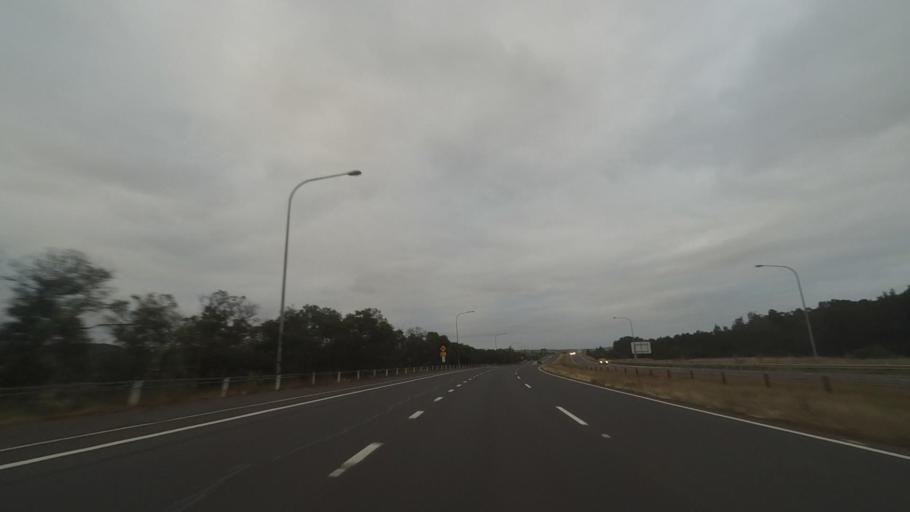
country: AU
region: New South Wales
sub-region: Shellharbour
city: Croom
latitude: -34.6122
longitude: 150.8370
